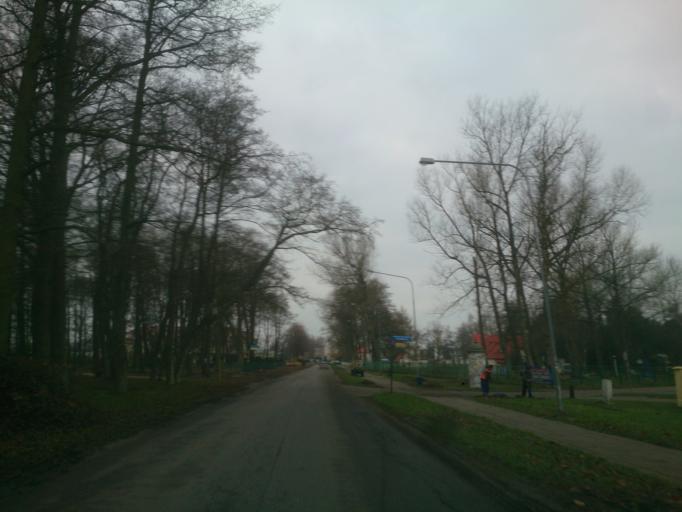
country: PL
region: West Pomeranian Voivodeship
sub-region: Powiat slawienski
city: Darlowo
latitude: 54.3845
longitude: 16.3234
